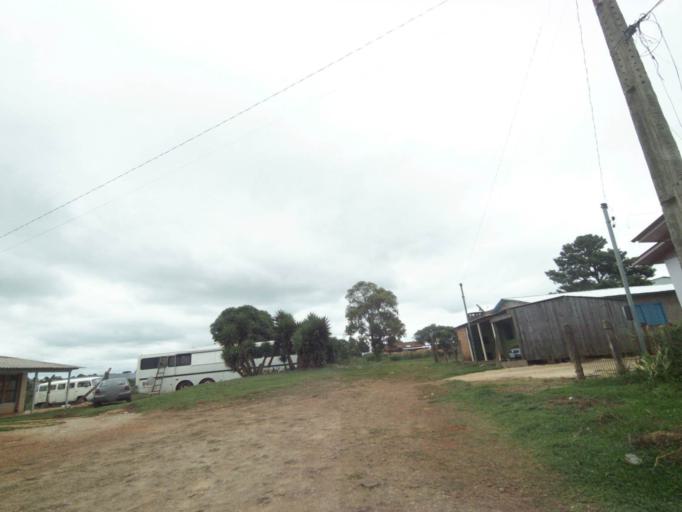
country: BR
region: Rio Grande do Sul
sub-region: Lagoa Vermelha
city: Lagoa Vermelha
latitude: -28.2132
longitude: -51.5074
